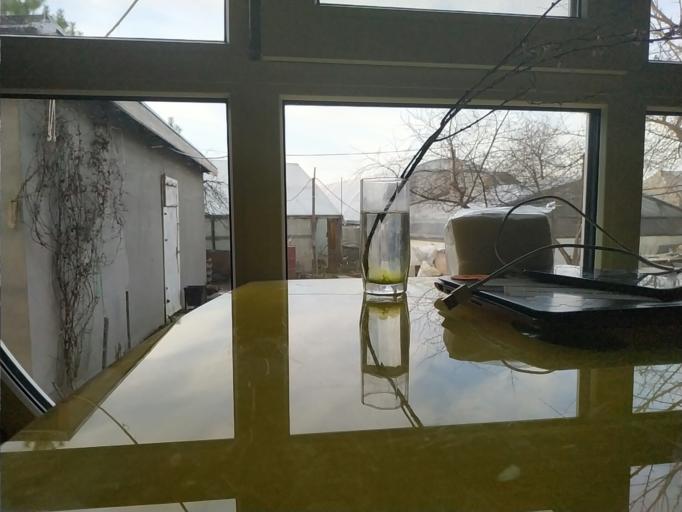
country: RU
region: Republic of Karelia
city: Suoyarvi
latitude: 61.9280
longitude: 32.2425
